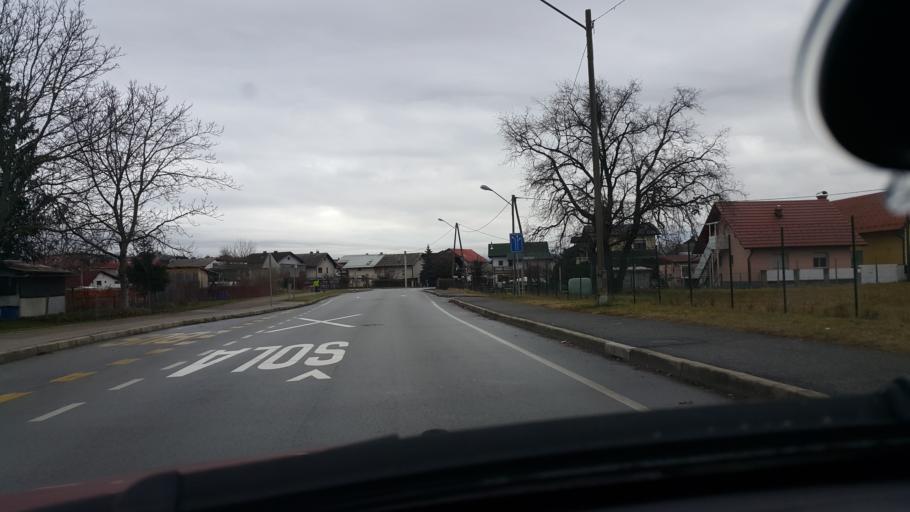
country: SI
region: Maribor
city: Maribor
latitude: 46.5344
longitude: 15.6735
